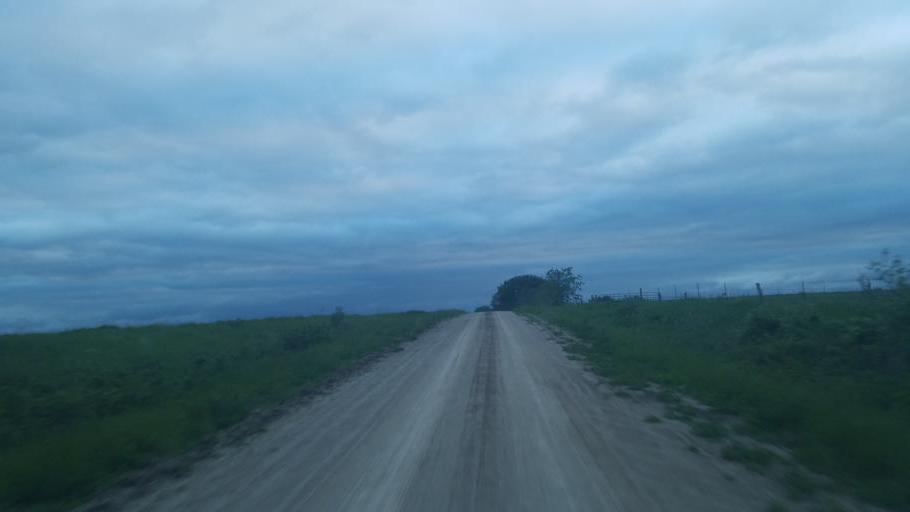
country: US
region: Iowa
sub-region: Decatur County
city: Lamoni
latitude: 40.5947
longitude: -93.9617
